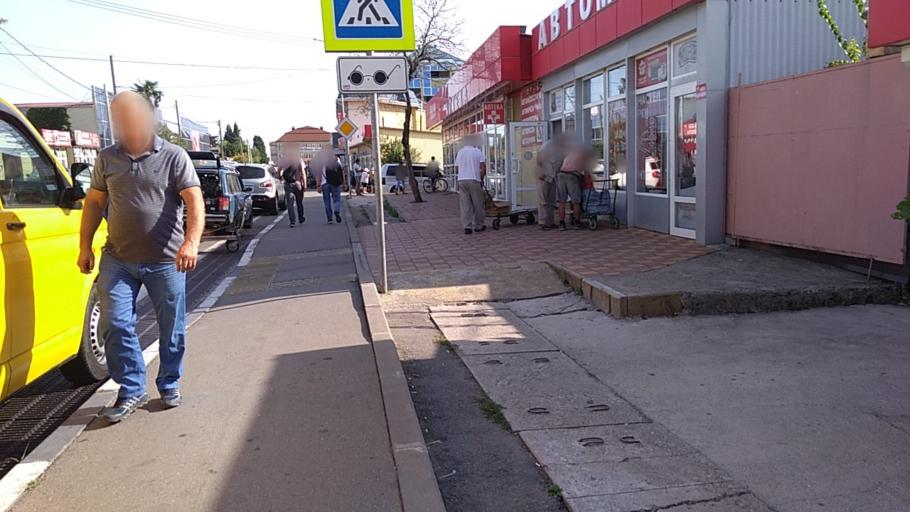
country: RU
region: Krasnodarskiy
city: Vysokoye
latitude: 43.3984
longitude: 40.0037
